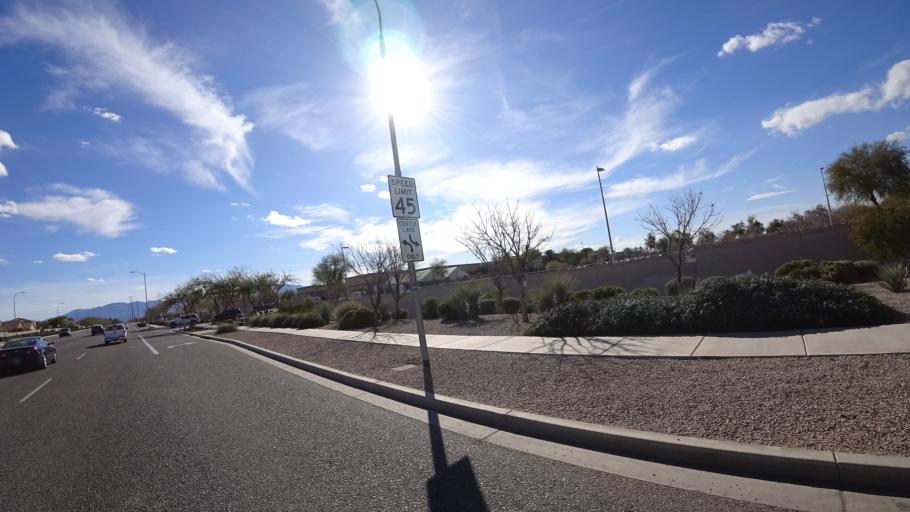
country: US
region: Arizona
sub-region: Maricopa County
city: Tolleson
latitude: 33.4218
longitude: -112.2213
